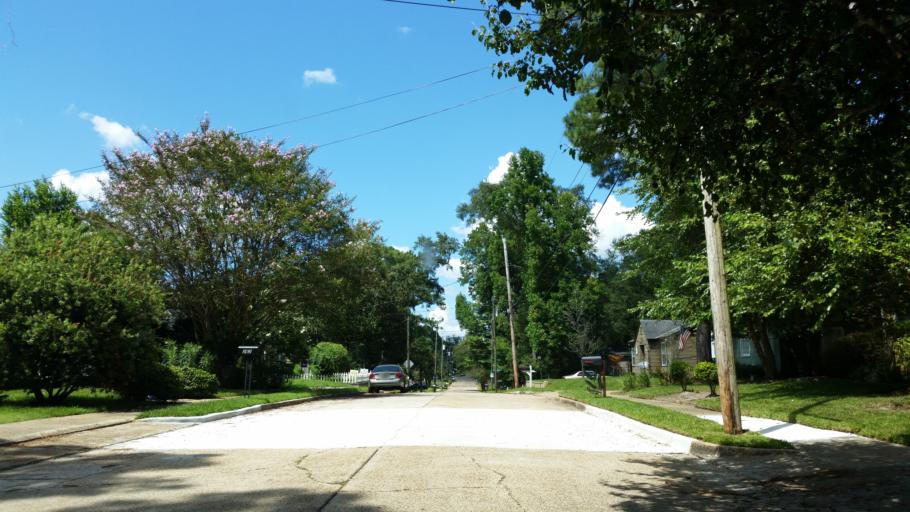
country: US
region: Alabama
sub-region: Mobile County
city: Mobile
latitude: 30.6776
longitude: -88.0967
